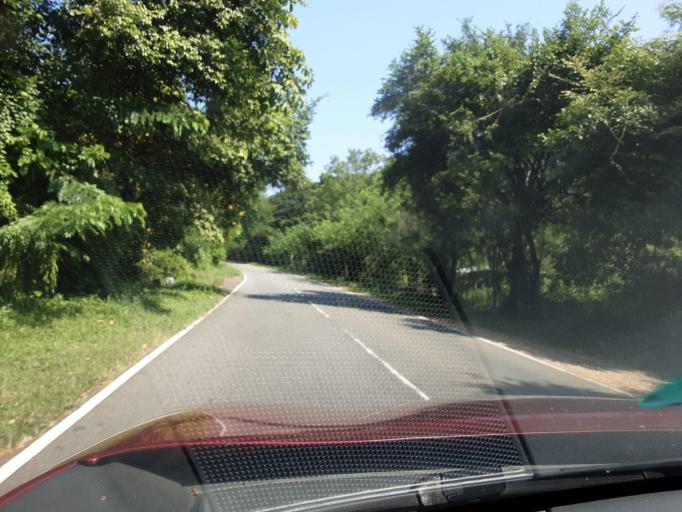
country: LK
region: Uva
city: Badulla
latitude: 7.2693
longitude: 81.0523
